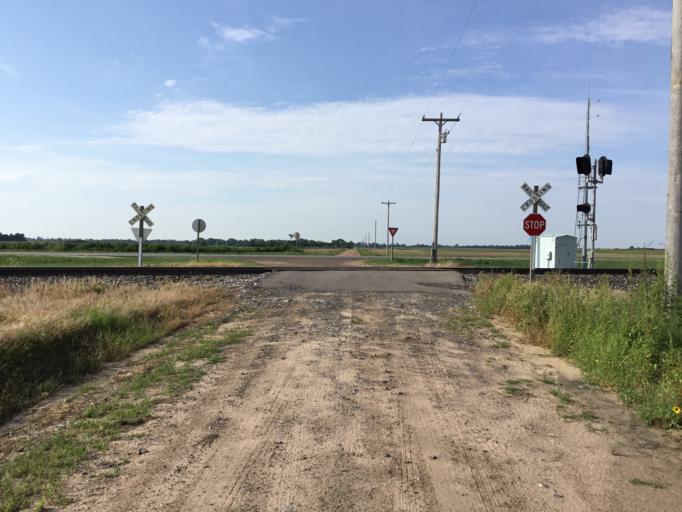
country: US
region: Kansas
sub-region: Stafford County
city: Stafford
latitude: 37.7824
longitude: -98.5018
